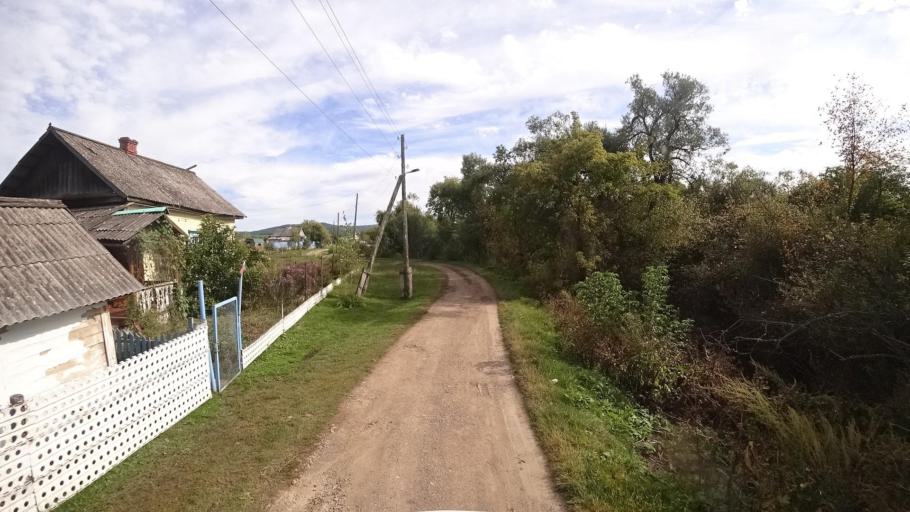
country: RU
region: Primorskiy
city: Dostoyevka
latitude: 44.3201
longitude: 133.4764
